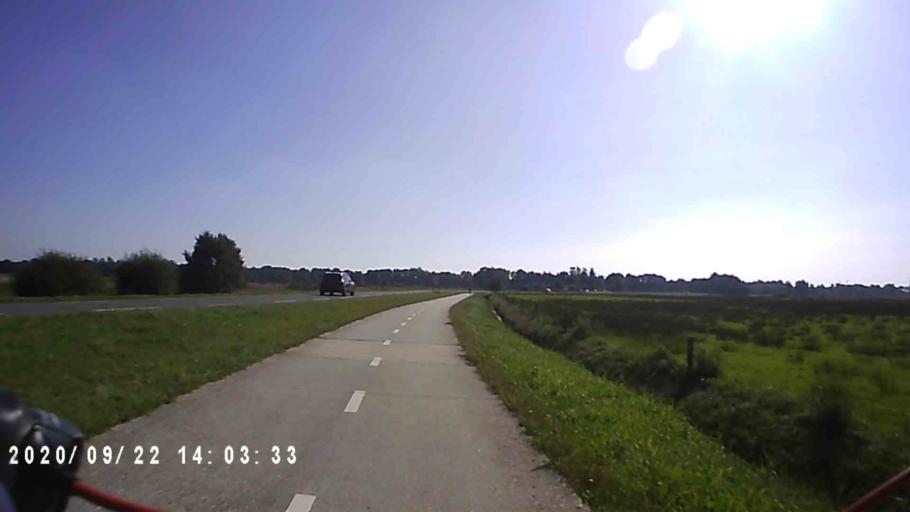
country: NL
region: Groningen
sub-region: Gemeente Leek
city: Leek
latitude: 53.1030
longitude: 6.4310
